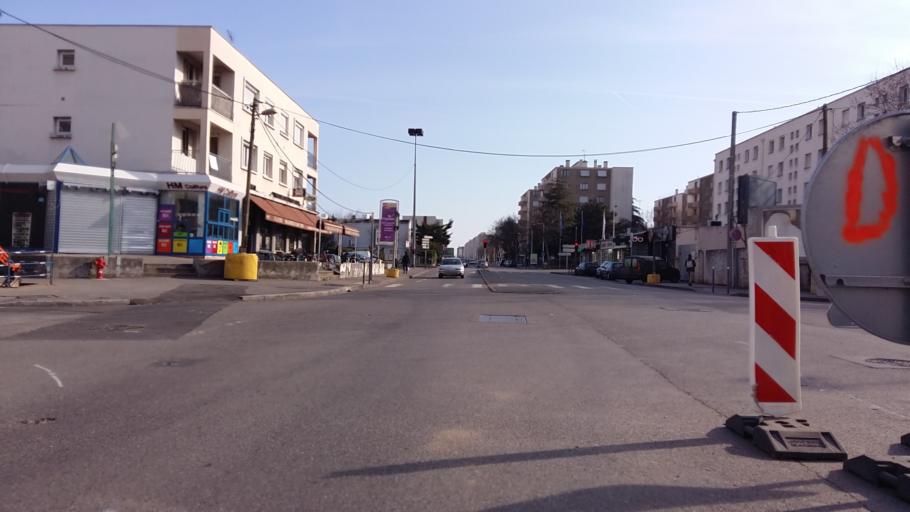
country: FR
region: Rhone-Alpes
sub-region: Departement du Rhone
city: Saint-Fons
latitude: 45.7276
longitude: 4.8619
